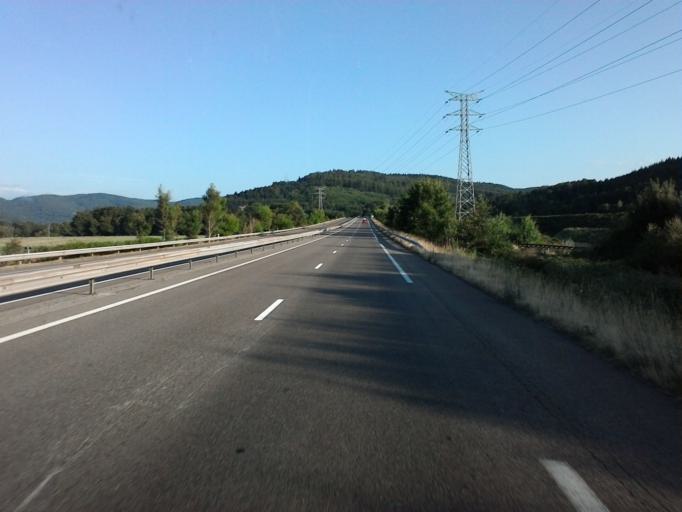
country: FR
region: Lorraine
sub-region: Departement des Vosges
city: Pouxeux
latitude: 48.1020
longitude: 6.5889
